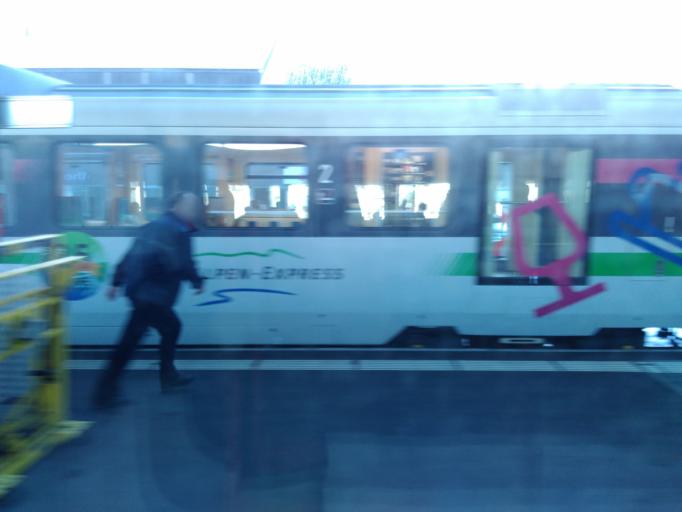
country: CH
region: Schwyz
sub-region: Bezirk Schwyz
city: Rothenthurm
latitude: 47.1058
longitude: 8.6745
